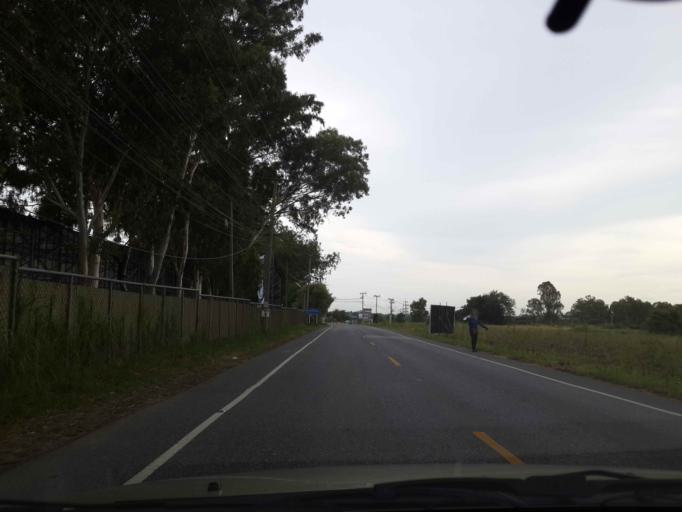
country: TH
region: Chon Buri
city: Phatthaya
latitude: 12.9219
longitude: 101.0061
